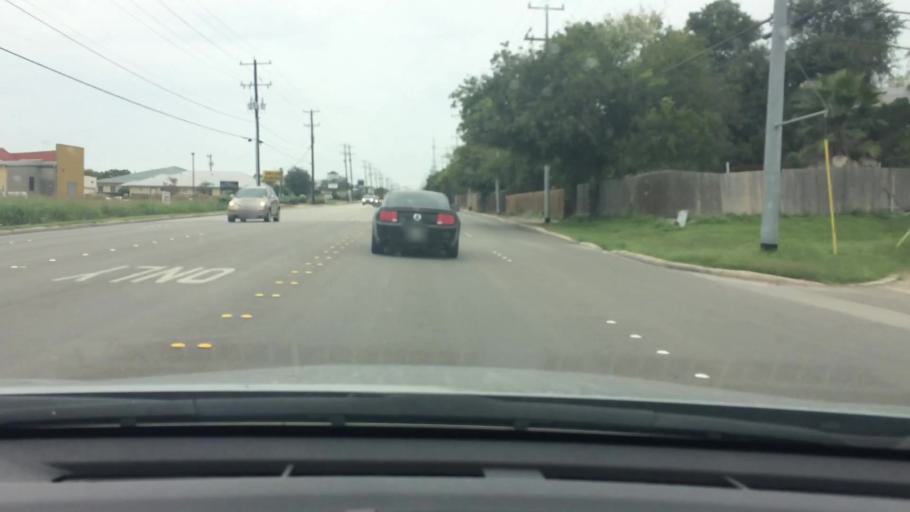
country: US
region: Texas
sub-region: Bexar County
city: Live Oak
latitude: 29.5402
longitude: -98.3381
